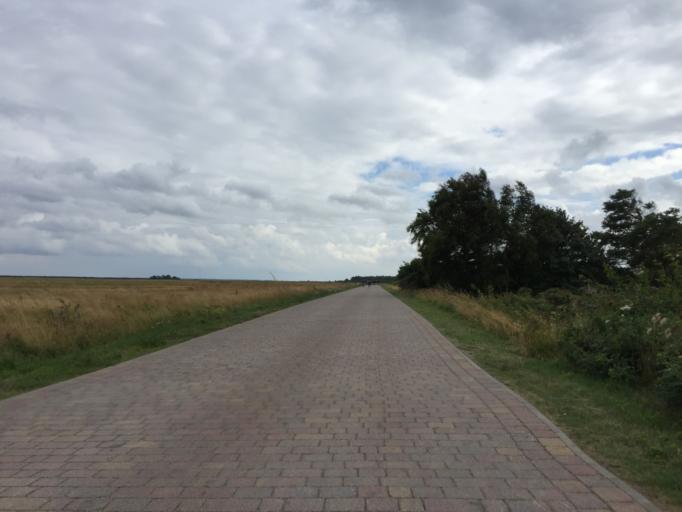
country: DE
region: Mecklenburg-Vorpommern
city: Hiddensee
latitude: 54.5593
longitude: 13.1084
